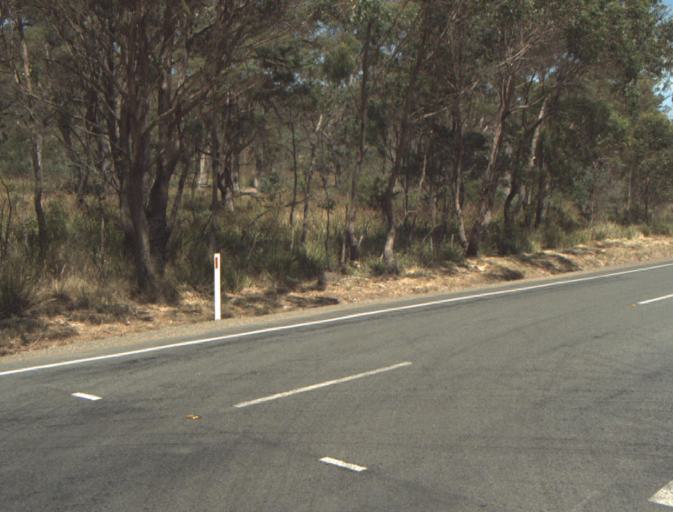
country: AU
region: Tasmania
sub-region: Launceston
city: Mayfield
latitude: -41.3397
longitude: 147.1441
